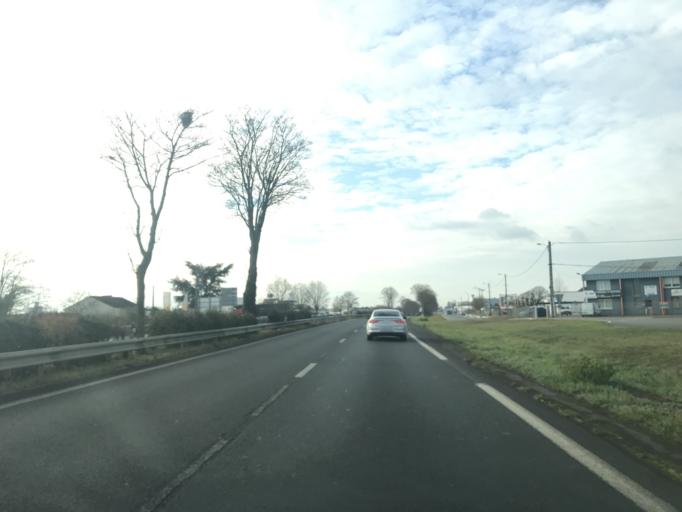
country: FR
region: Poitou-Charentes
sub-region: Departement des Deux-Sevres
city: Chauray
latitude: 46.3418
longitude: -0.3869
